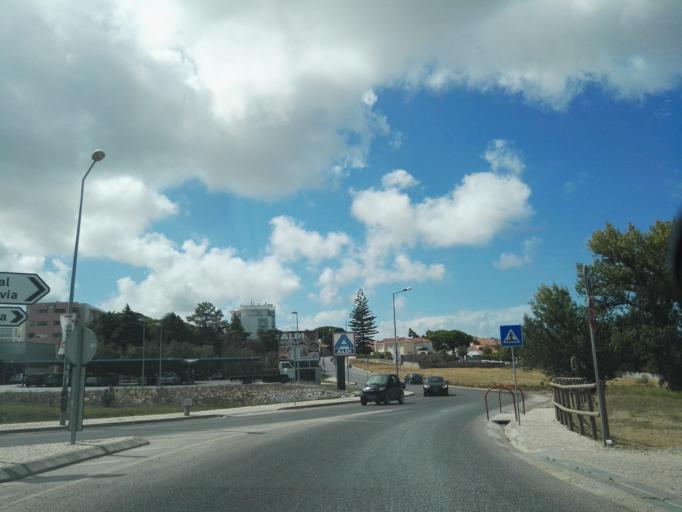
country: PT
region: Setubal
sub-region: Sesimbra
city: Sesimbra
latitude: 38.4654
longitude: -9.0973
